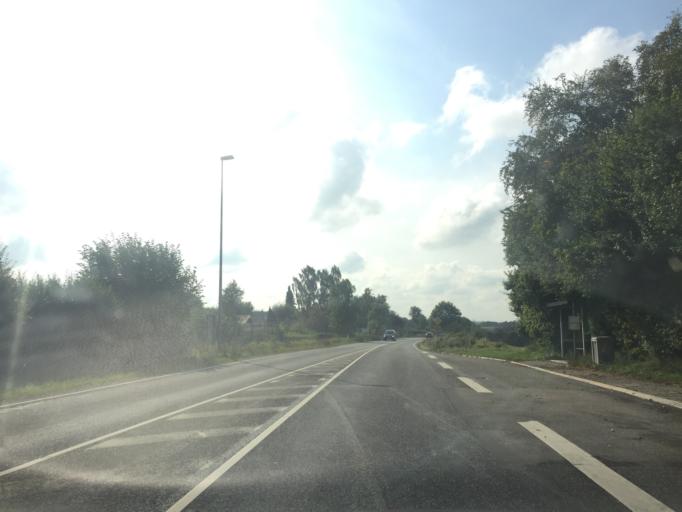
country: DK
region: Zealand
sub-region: Lejre Kommune
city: Ejby
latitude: 55.6565
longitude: 11.8183
